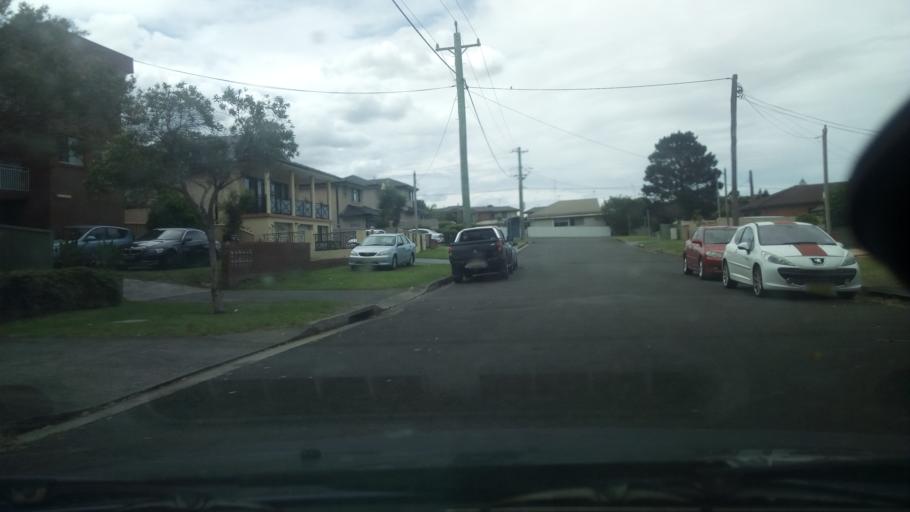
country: AU
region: New South Wales
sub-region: Wollongong
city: Mangerton
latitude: -34.4354
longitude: 150.8824
